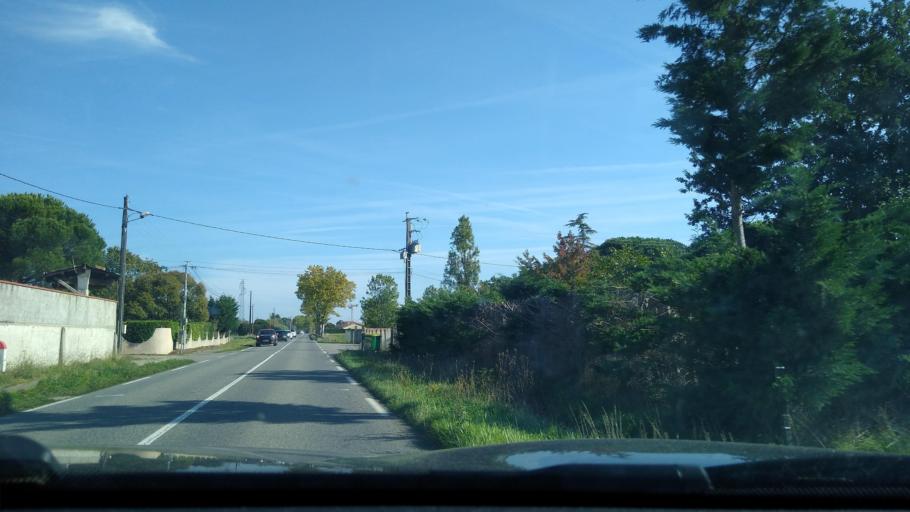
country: FR
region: Midi-Pyrenees
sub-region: Departement de la Haute-Garonne
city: Mondonville
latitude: 43.6765
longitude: 1.2715
